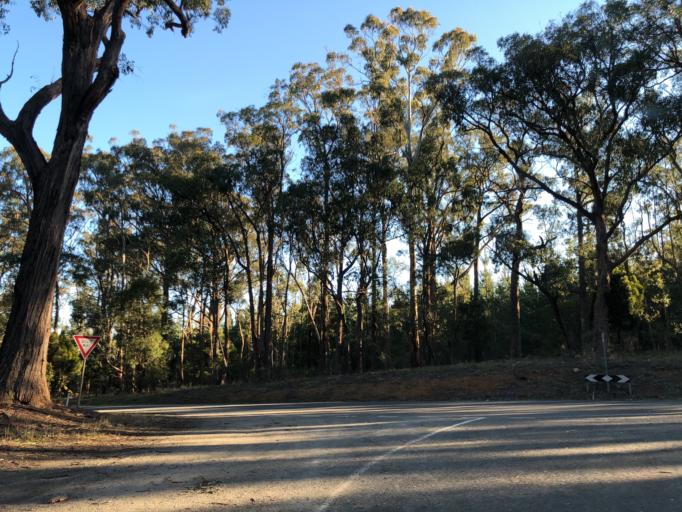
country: AU
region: Victoria
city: Brown Hill
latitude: -37.5131
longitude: 144.1622
